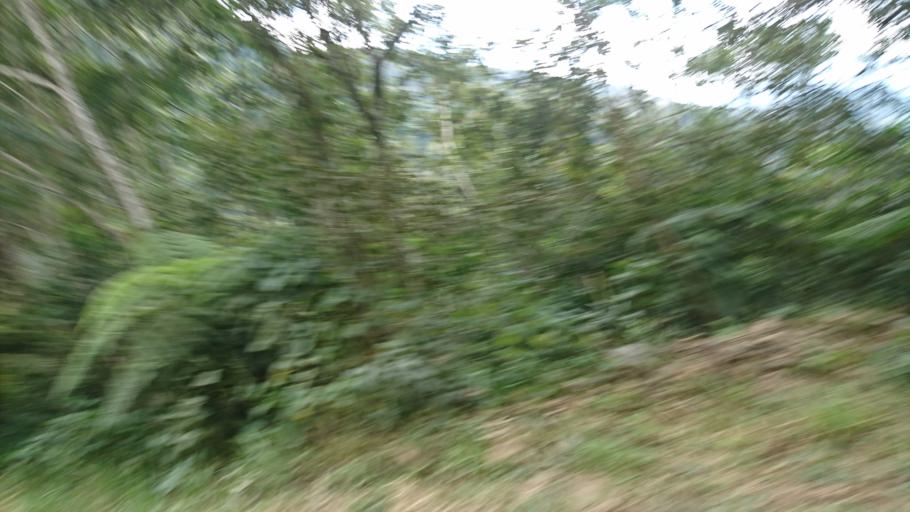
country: BO
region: La Paz
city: Coroico
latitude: -16.1131
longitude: -67.7864
